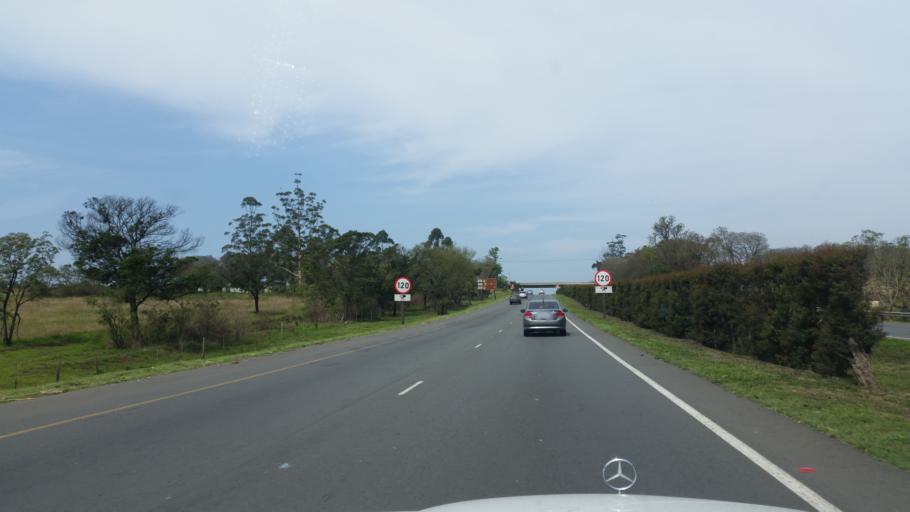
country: ZA
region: KwaZulu-Natal
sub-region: uMgungundlovu District Municipality
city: Camperdown
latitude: -29.7303
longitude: 30.5492
